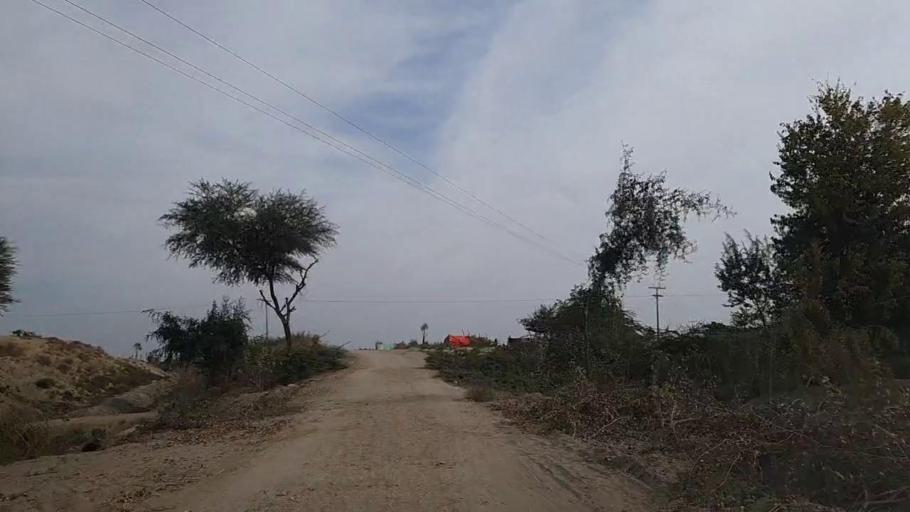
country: PK
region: Sindh
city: Jam Sahib
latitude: 26.4405
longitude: 68.5814
